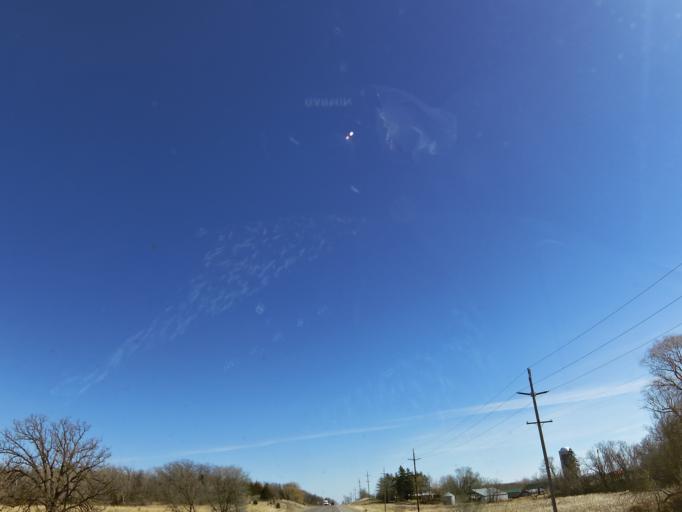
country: US
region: Minnesota
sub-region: Wright County
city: Maple Lake
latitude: 45.2179
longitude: -93.9497
